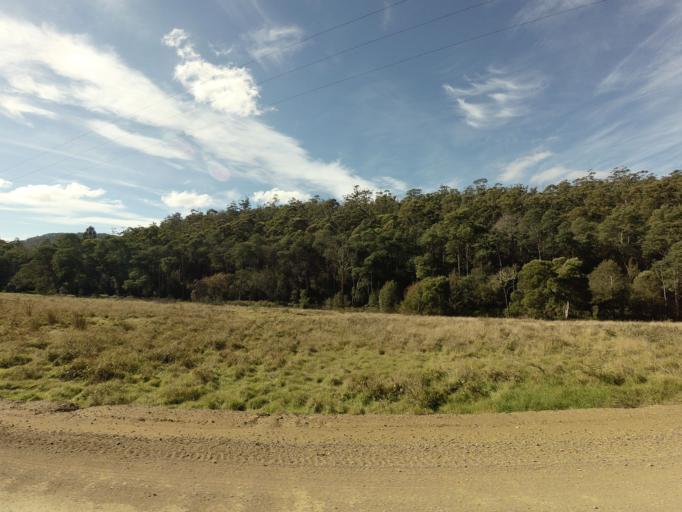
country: AU
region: Tasmania
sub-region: Clarence
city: Sandford
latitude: -43.1297
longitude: 147.7637
